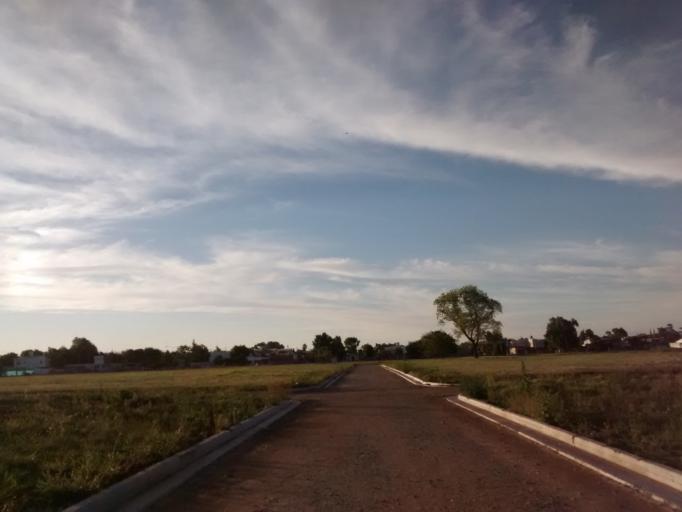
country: AR
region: Buenos Aires
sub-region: Partido de La Plata
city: La Plata
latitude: -34.9520
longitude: -57.9394
